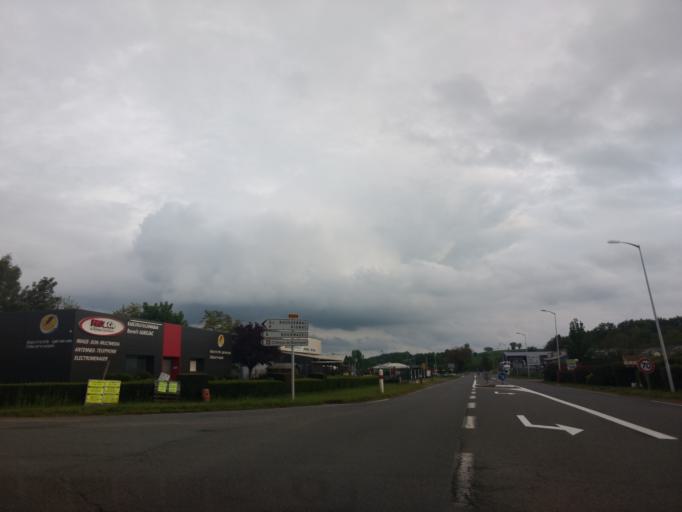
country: FR
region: Midi-Pyrenees
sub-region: Departement de l'Aveyron
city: Montbazens
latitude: 44.4610
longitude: 2.2224
